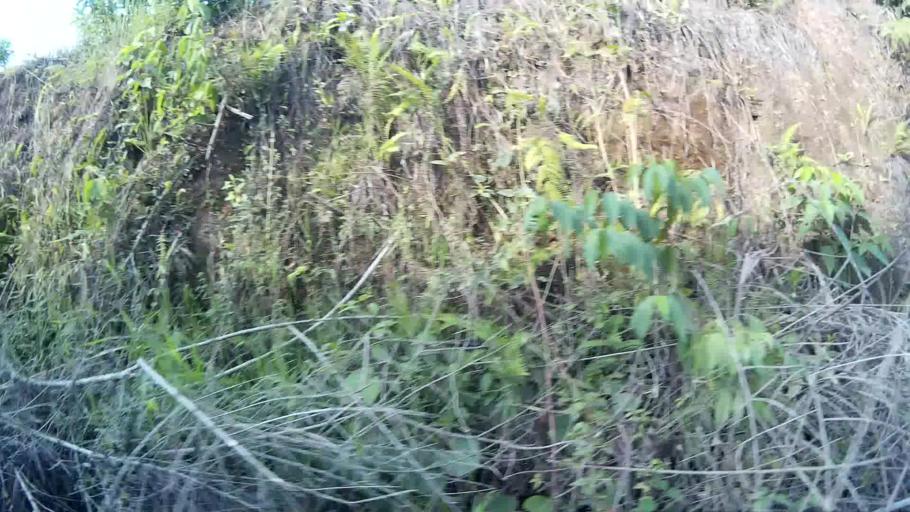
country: CO
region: Valle del Cauca
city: Ulloa
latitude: 4.7521
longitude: -75.7441
